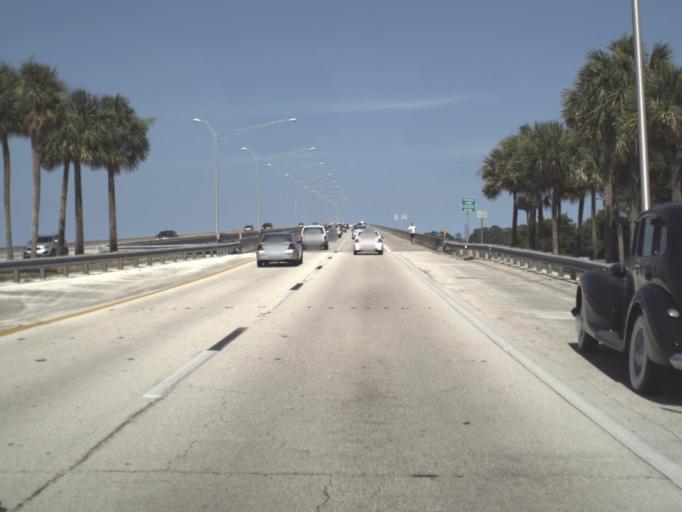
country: US
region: Florida
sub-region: Saint Johns County
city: Saint Augustine South
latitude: 29.8669
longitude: -81.3147
